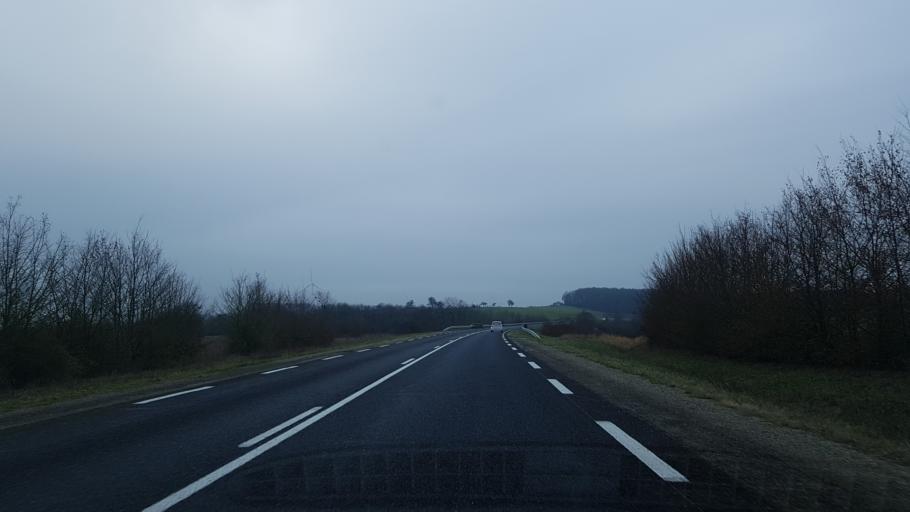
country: FR
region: Lorraine
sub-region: Departement de la Moselle
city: Gros-Rederching
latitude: 49.0960
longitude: 7.2145
